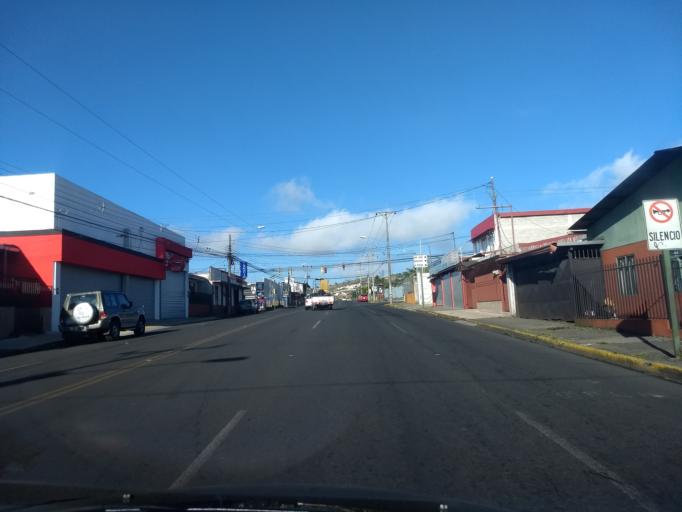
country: CR
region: Alajuela
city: San Ramon
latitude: 10.0919
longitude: -84.4685
